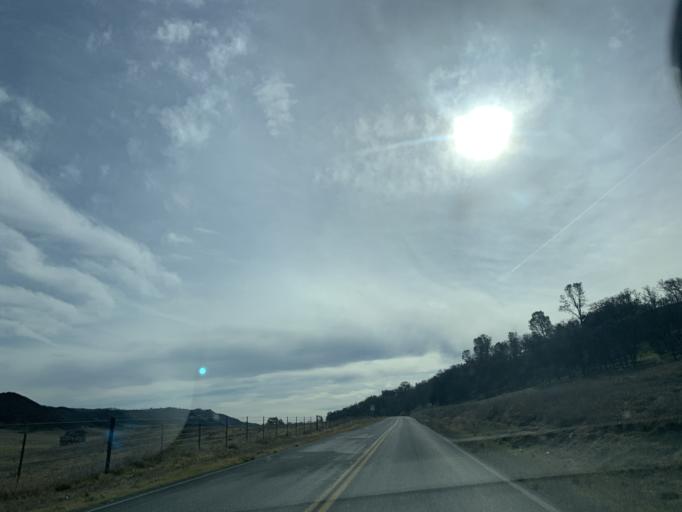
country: US
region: California
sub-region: Monterey County
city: Greenfield
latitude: 36.4983
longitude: -121.0848
